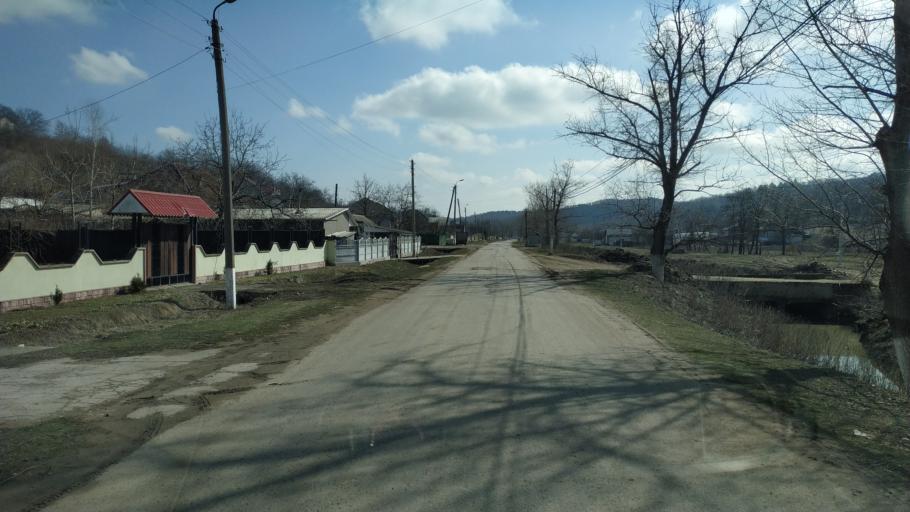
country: MD
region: Hincesti
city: Hincesti
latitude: 46.8779
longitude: 28.6277
